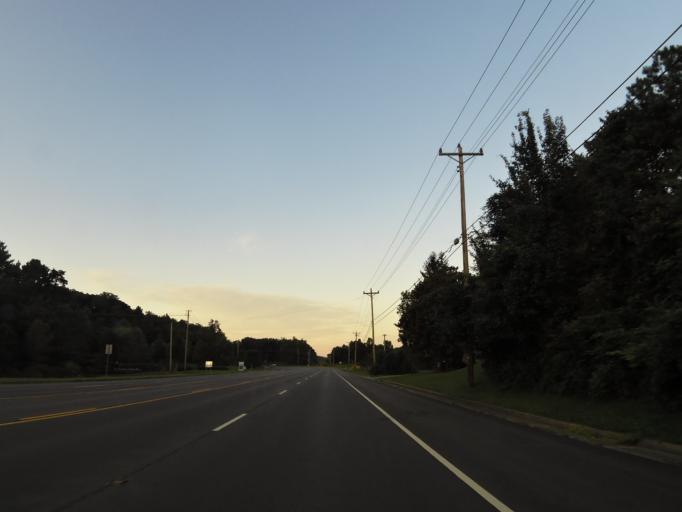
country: US
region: Tennessee
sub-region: Roane County
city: Kingston
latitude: 35.8998
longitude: -84.4034
